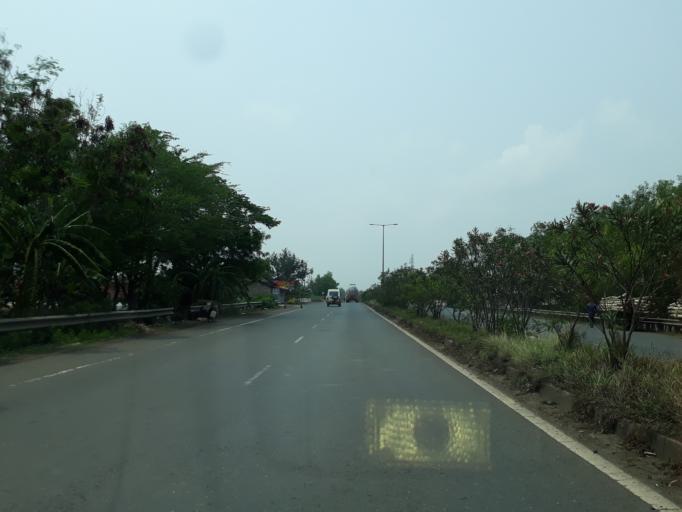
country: IN
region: West Bengal
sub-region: Purba Medinipur
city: Mahishadal
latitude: 22.1231
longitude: 87.9976
